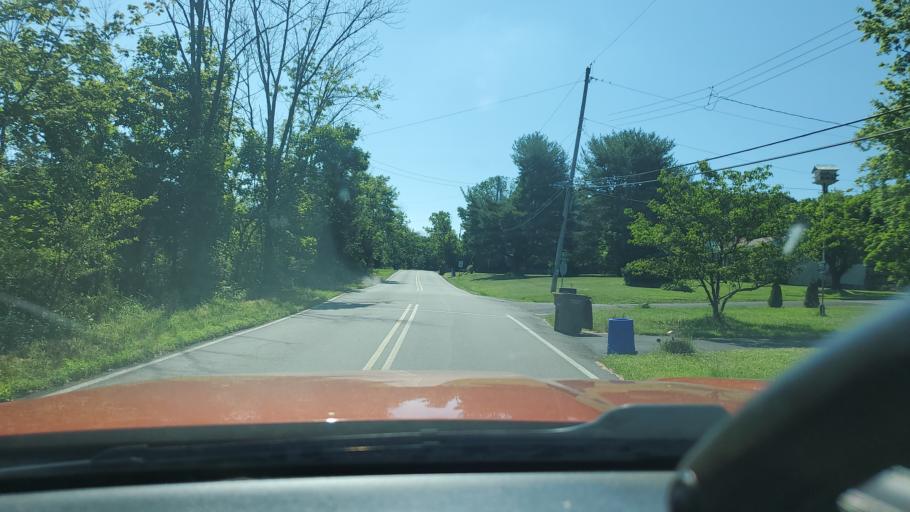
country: US
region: Pennsylvania
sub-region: Montgomery County
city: Red Hill
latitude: 40.3509
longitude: -75.5222
